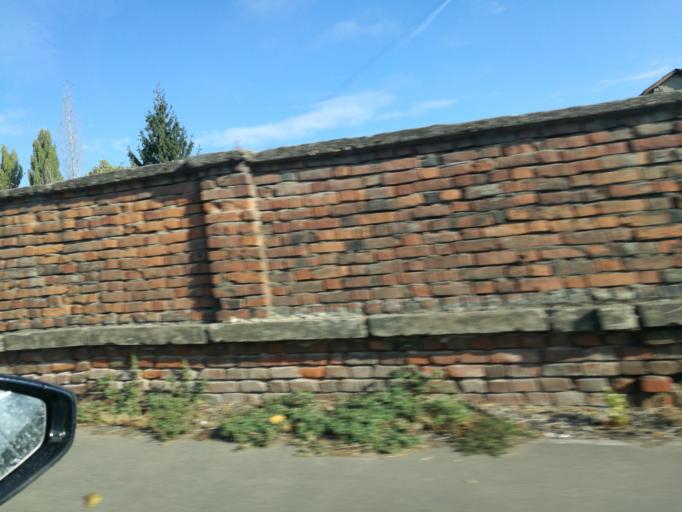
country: RO
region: Bihor
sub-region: Comuna Biharea
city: Oradea
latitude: 47.0420
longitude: 21.9229
